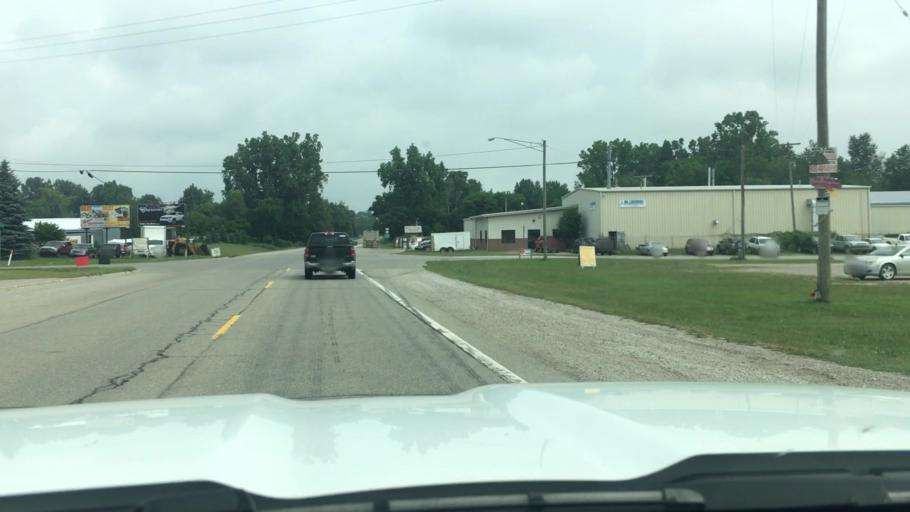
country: US
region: Michigan
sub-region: Sanilac County
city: Brown City
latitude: 43.1522
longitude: -83.0751
